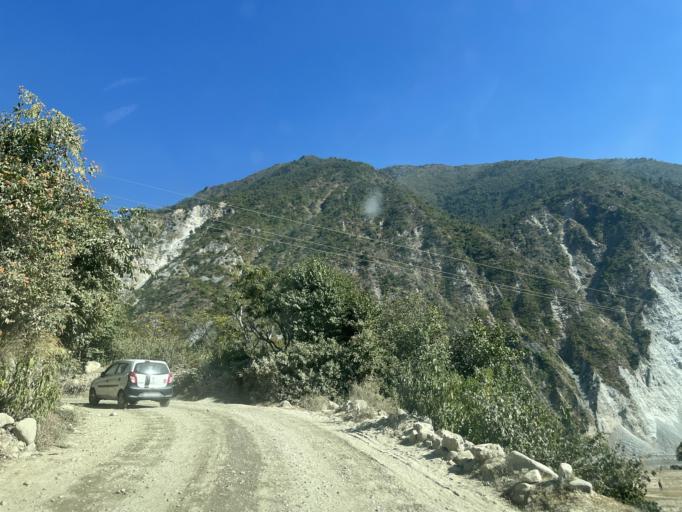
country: IN
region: Uttarakhand
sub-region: Almora
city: Ranikhet
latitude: 29.5507
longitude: 79.4021
